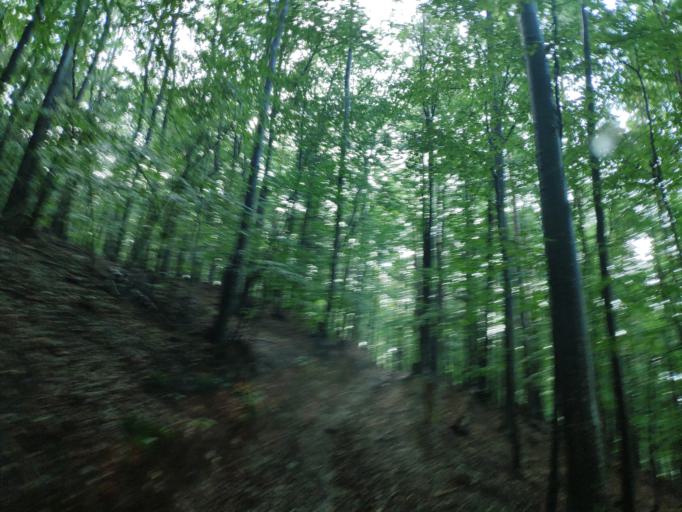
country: SK
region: Kosicky
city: Medzev
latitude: 48.7483
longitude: 20.9991
